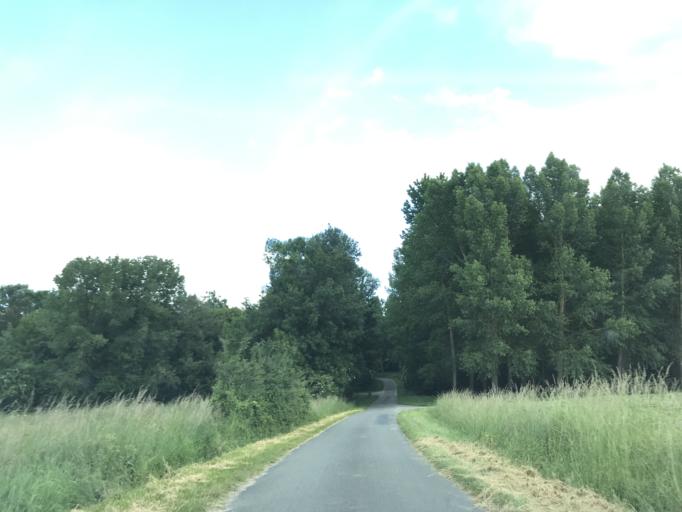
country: FR
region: Aquitaine
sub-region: Departement de la Dordogne
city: Saint-Aulaye
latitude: 45.2654
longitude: 0.1234
